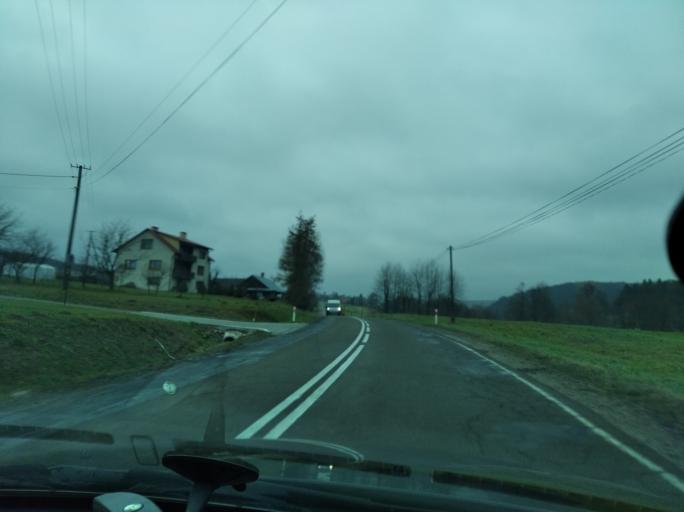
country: PL
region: Subcarpathian Voivodeship
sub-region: Powiat rzeszowski
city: Dynow
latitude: 49.8568
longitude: 22.2500
